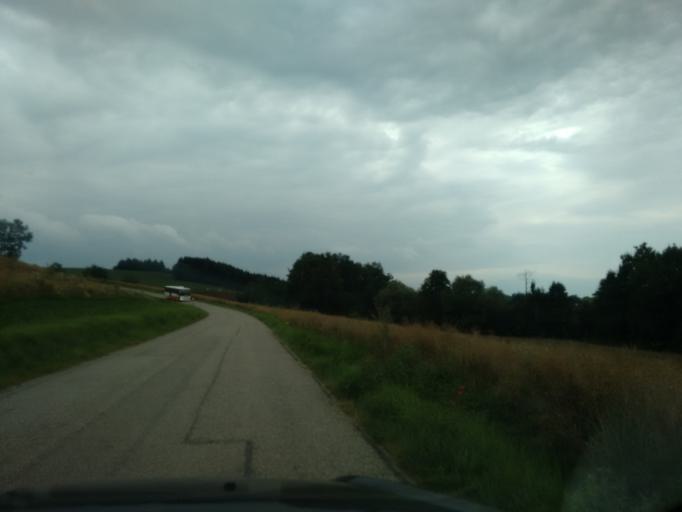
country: AT
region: Upper Austria
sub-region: Politischer Bezirk Grieskirchen
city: Bad Schallerbach
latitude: 48.2009
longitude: 13.9574
